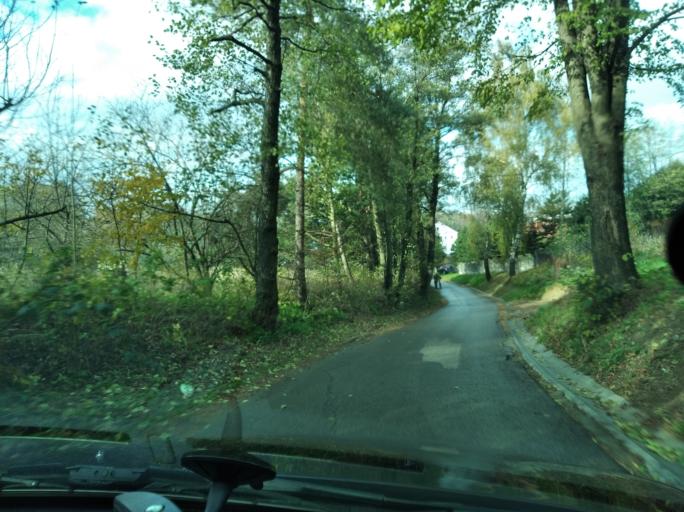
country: PL
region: Subcarpathian Voivodeship
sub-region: Powiat debicki
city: Debica
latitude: 50.0397
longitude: 21.4482
